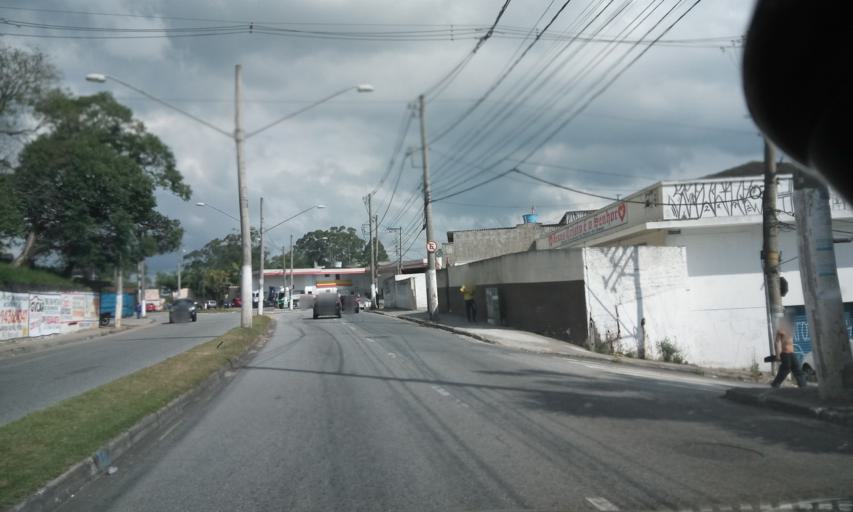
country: BR
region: Sao Paulo
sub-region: Sao Bernardo Do Campo
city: Sao Bernardo do Campo
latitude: -23.7543
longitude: -46.5747
